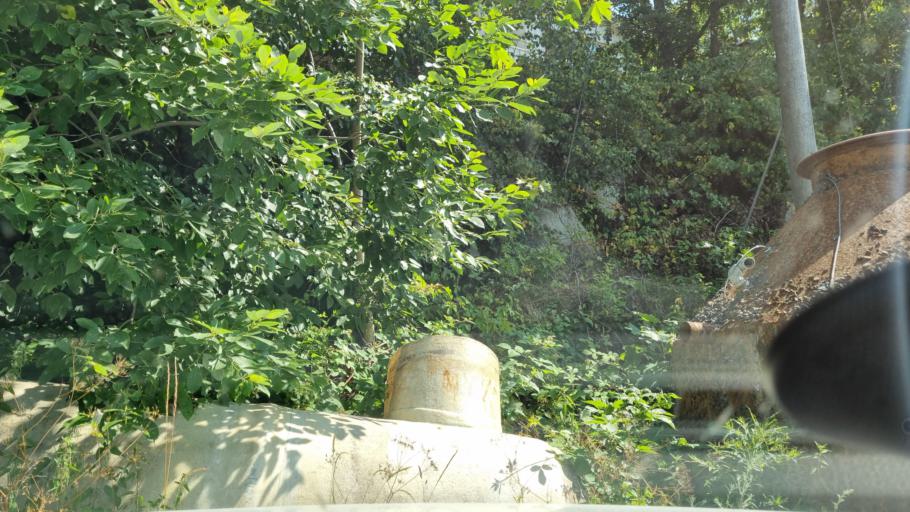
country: NO
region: Aust-Agder
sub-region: Arendal
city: Arendal
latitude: 58.4568
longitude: 8.8188
